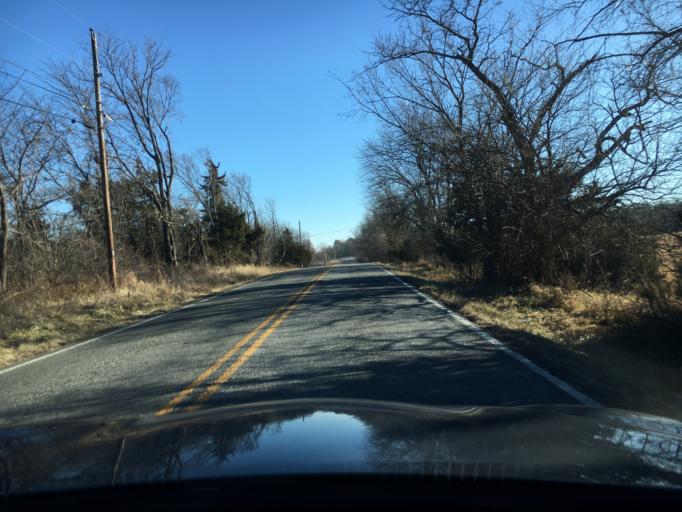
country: US
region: Missouri
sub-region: Cass County
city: Belton
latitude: 38.8036
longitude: -94.6726
